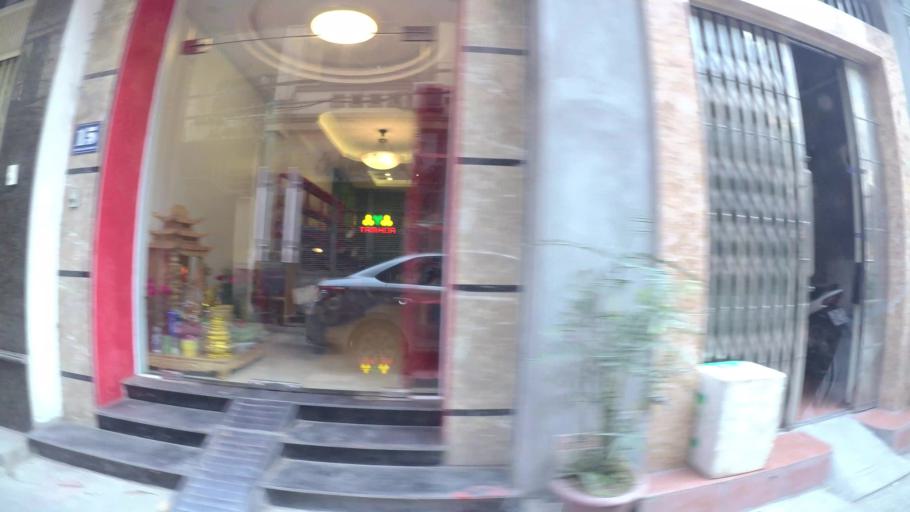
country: VN
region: Ha Noi
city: Tay Ho
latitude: 21.0513
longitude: 105.8065
